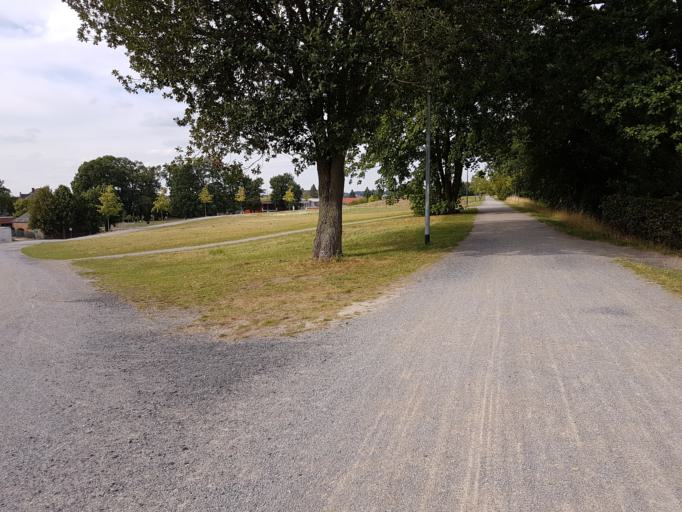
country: DE
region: North Rhine-Westphalia
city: Olfen
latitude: 51.7039
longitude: 7.3821
